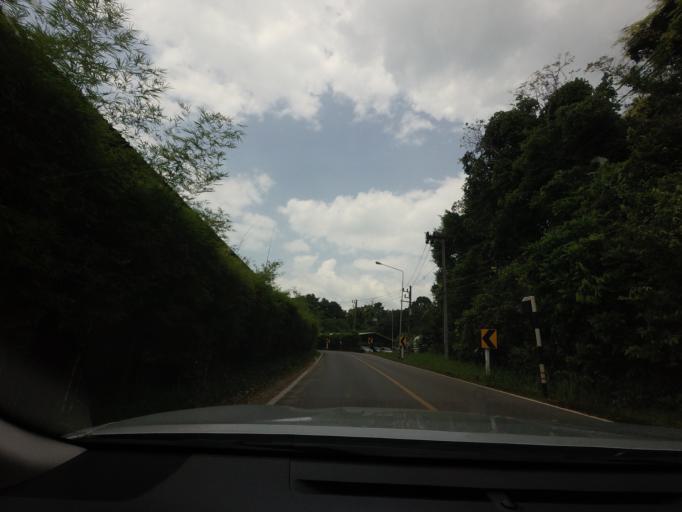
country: TH
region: Phangnga
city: Ban Ao Nang
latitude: 8.0846
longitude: 98.7467
